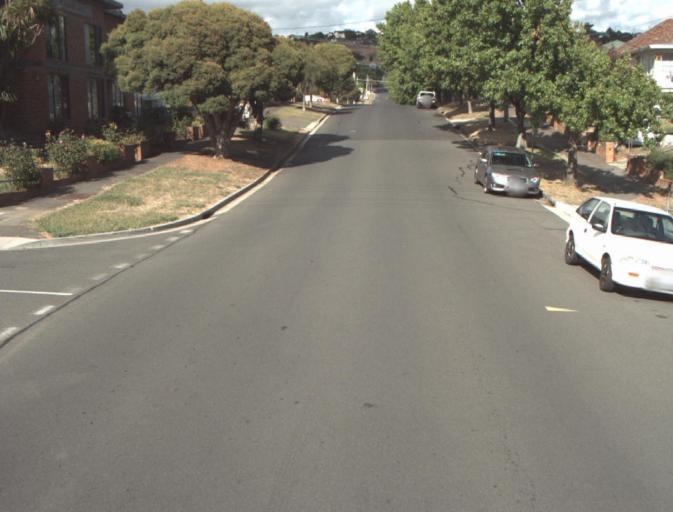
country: AU
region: Tasmania
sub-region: Launceston
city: Newstead
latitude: -41.4490
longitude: 147.1640
